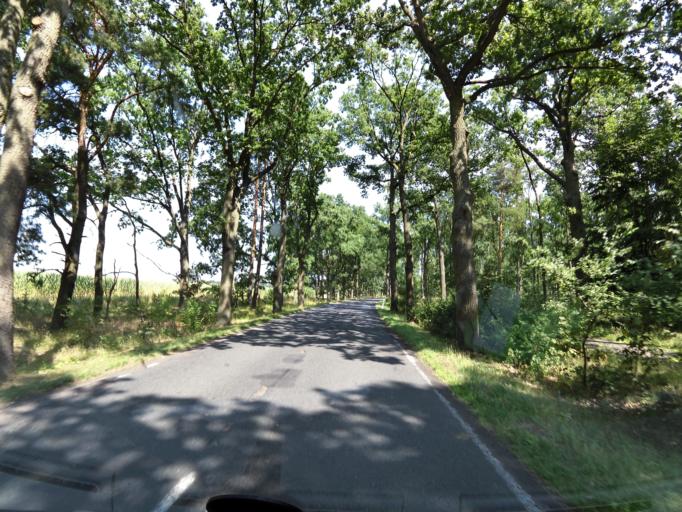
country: DE
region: Brandenburg
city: Liebenwalde
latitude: 52.8379
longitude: 13.3128
